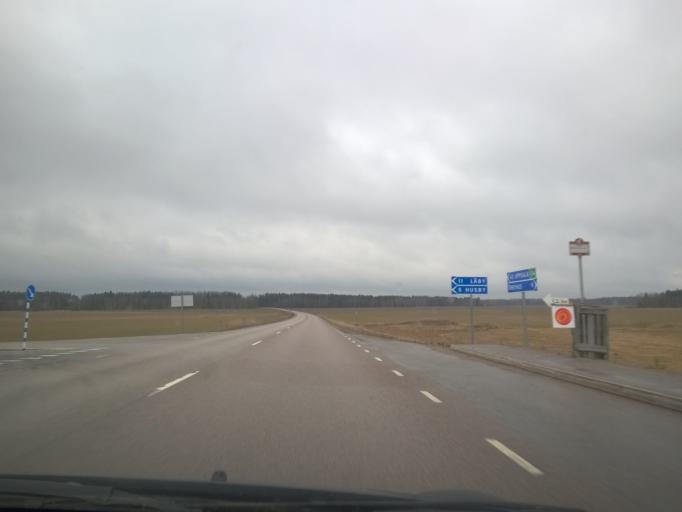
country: SE
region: Uppsala
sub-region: Tierps Kommun
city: Orbyhus
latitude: 60.1775
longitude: 17.6221
